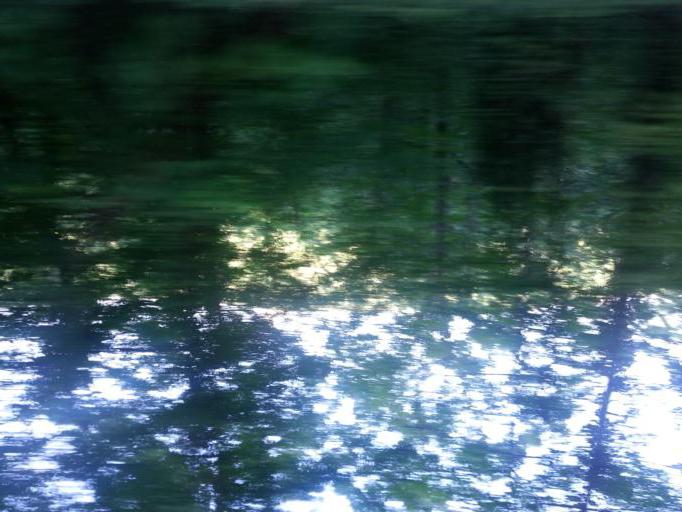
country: US
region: Tennessee
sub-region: Blount County
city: Maryville
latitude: 35.6647
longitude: -83.9068
